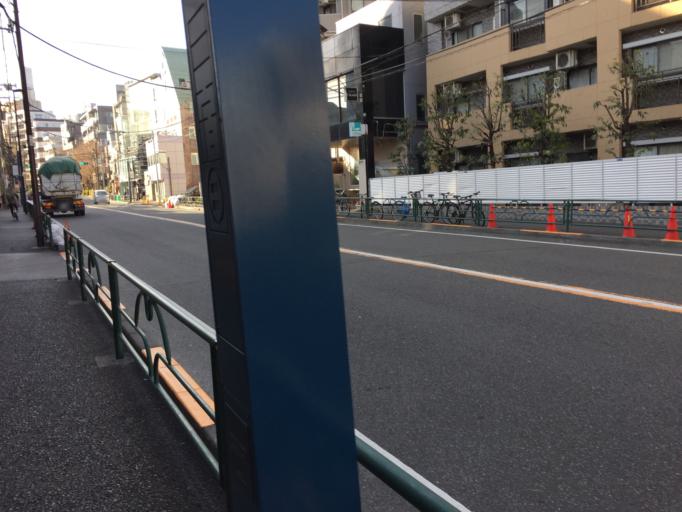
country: JP
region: Tokyo
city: Tokyo
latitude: 35.6493
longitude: 139.6778
